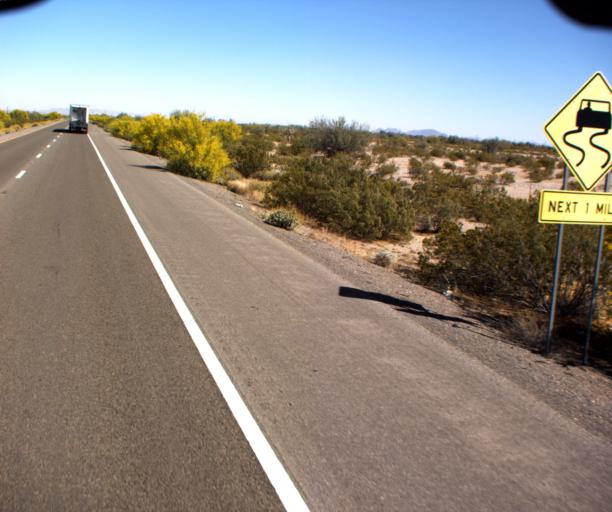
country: US
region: Arizona
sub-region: Pinal County
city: Maricopa
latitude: 32.8296
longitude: -112.0147
